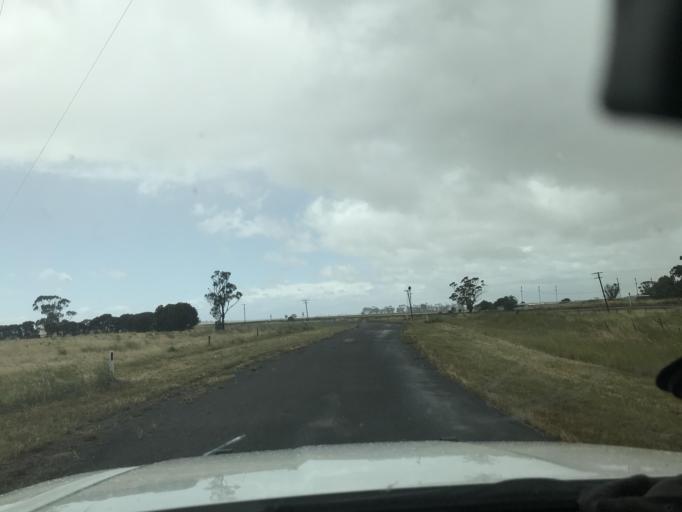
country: AU
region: South Australia
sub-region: Tatiara
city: Bordertown
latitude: -36.3744
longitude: 140.9894
